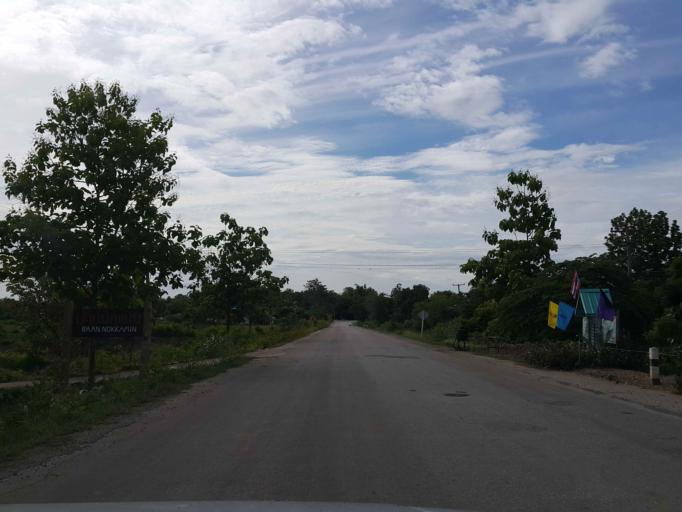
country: TH
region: Sukhothai
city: Thung Saliam
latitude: 17.2712
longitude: 99.5319
